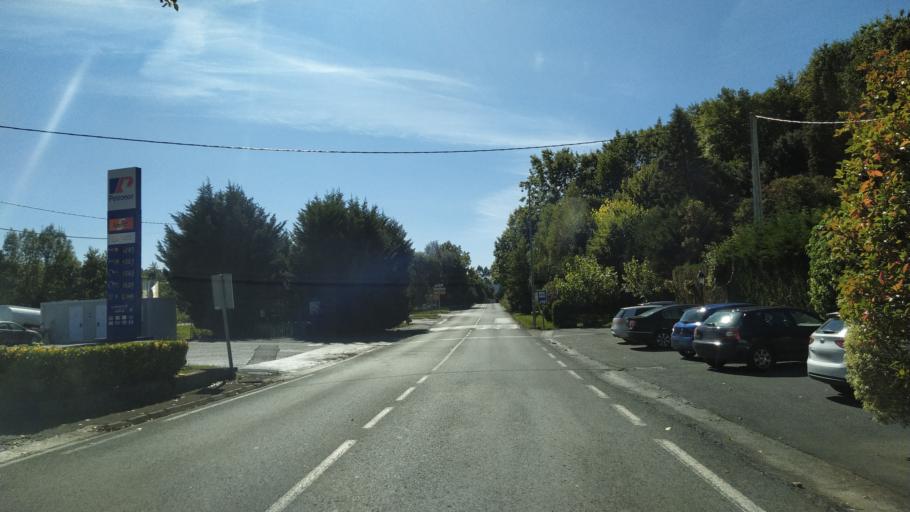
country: ES
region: Basque Country
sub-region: Bizkaia
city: Derio
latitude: 43.3186
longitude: -2.8769
